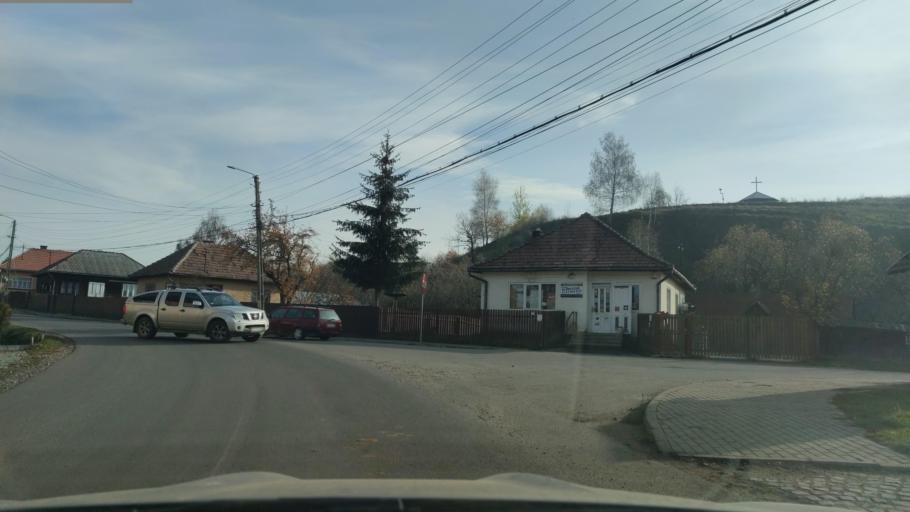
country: RO
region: Harghita
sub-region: Comuna Ditrau
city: Ditrau
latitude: 46.8080
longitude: 25.5068
